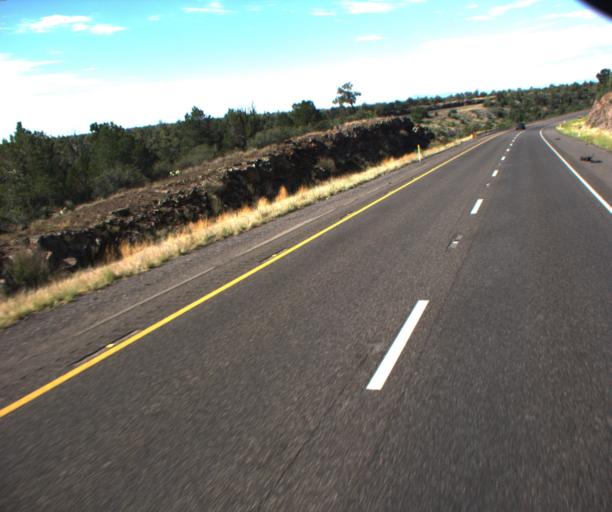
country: US
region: Arizona
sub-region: Yavapai County
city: Village of Oak Creek (Big Park)
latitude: 34.7721
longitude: -111.6399
